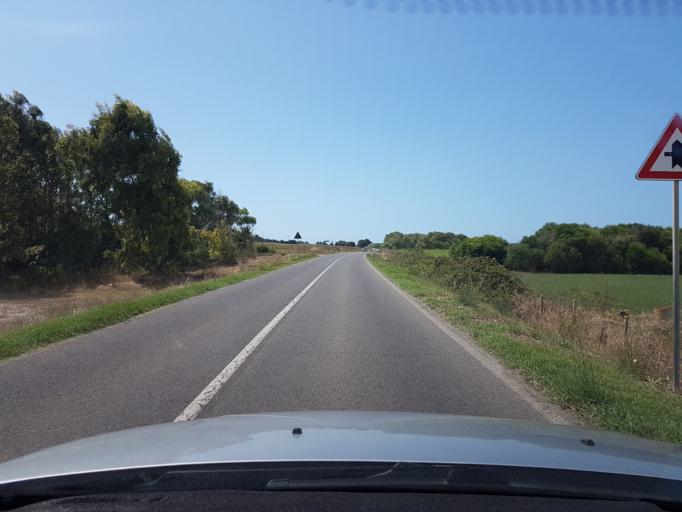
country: IT
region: Sardinia
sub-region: Provincia di Oristano
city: Riola Sardo
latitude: 40.0206
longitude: 8.4839
